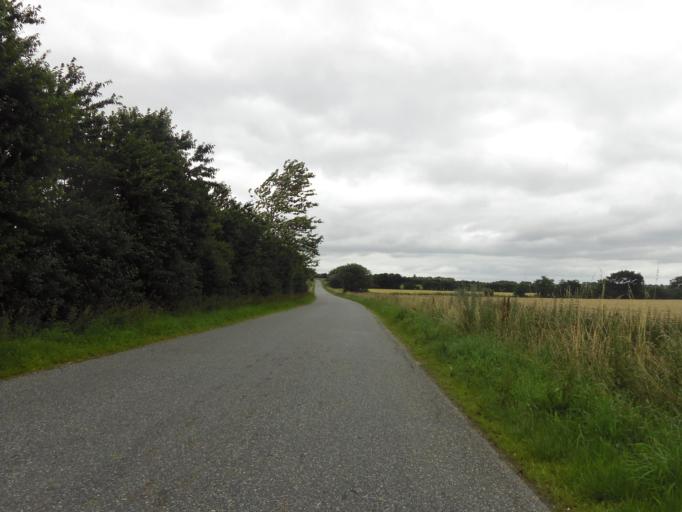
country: DK
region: South Denmark
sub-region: Haderslev Kommune
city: Gram
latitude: 55.2628
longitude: 9.1639
